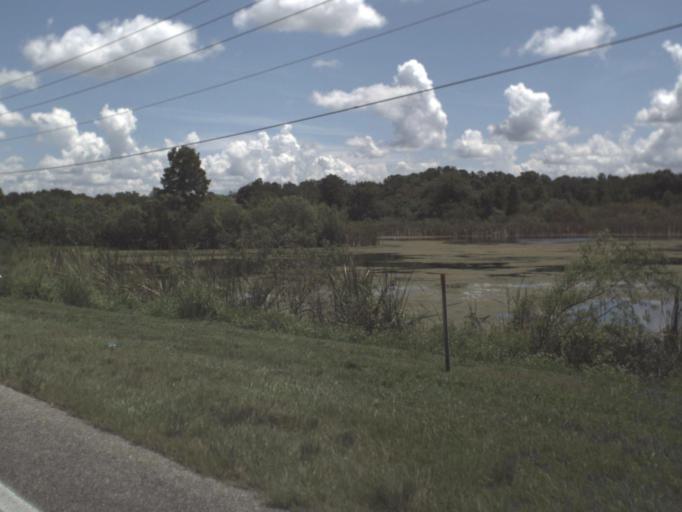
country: US
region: Florida
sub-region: Polk County
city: Fussels Corner
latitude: 28.0478
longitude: -81.8828
